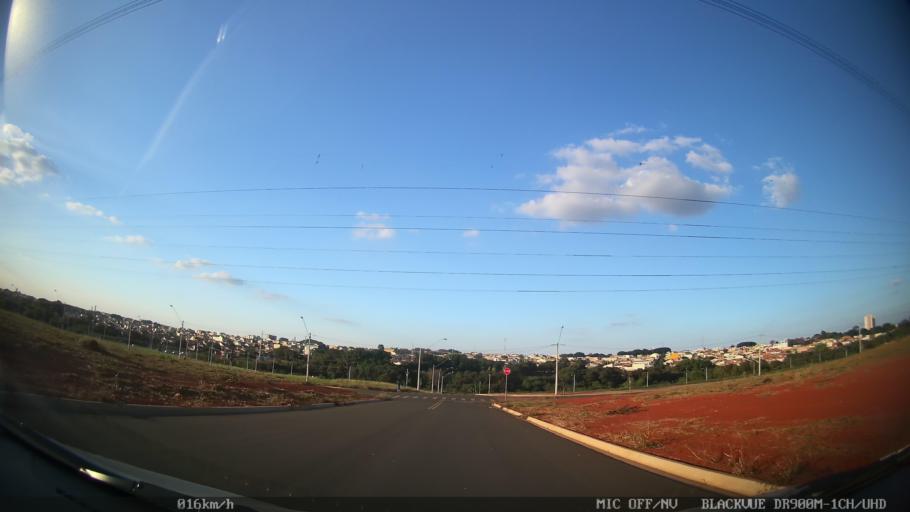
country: BR
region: Sao Paulo
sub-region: Santa Barbara D'Oeste
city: Santa Barbara d'Oeste
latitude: -22.7448
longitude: -47.3883
